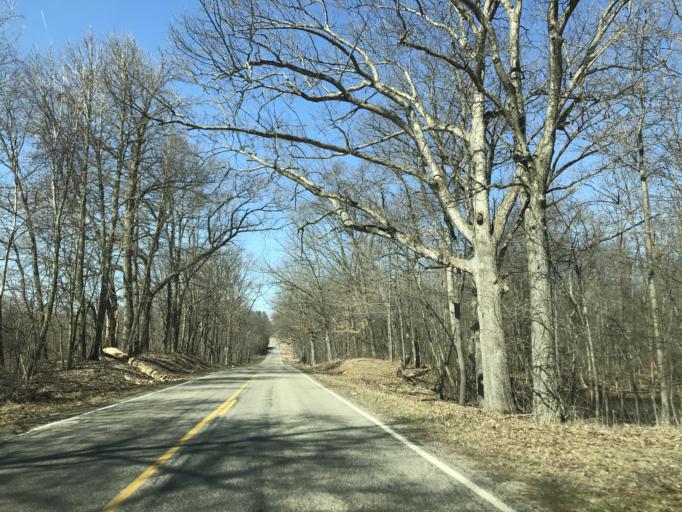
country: US
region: Michigan
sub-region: Hillsdale County
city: Litchfield
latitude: 41.9856
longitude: -84.7448
